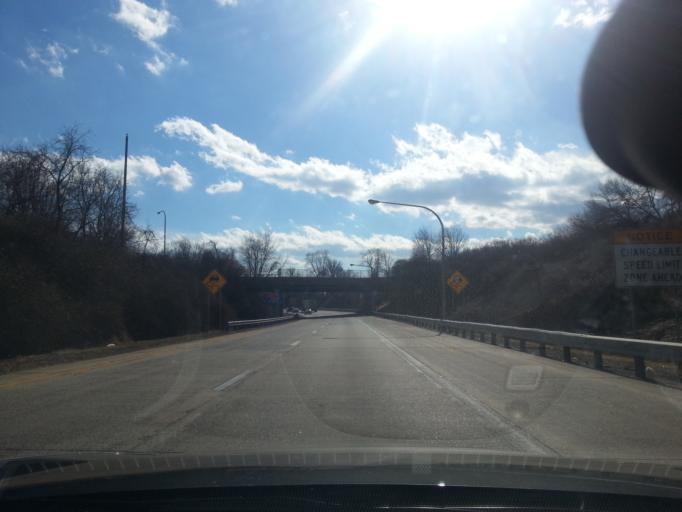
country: US
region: Delaware
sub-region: New Castle County
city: Claymont
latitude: 39.8166
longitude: -75.4533
